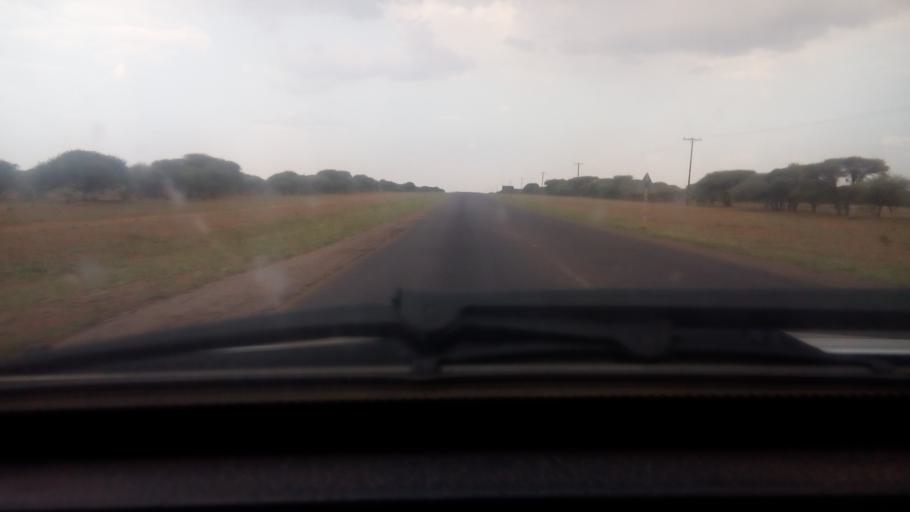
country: BW
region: Kweneng
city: Metsemotlhaba
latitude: -24.4680
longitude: 25.6791
